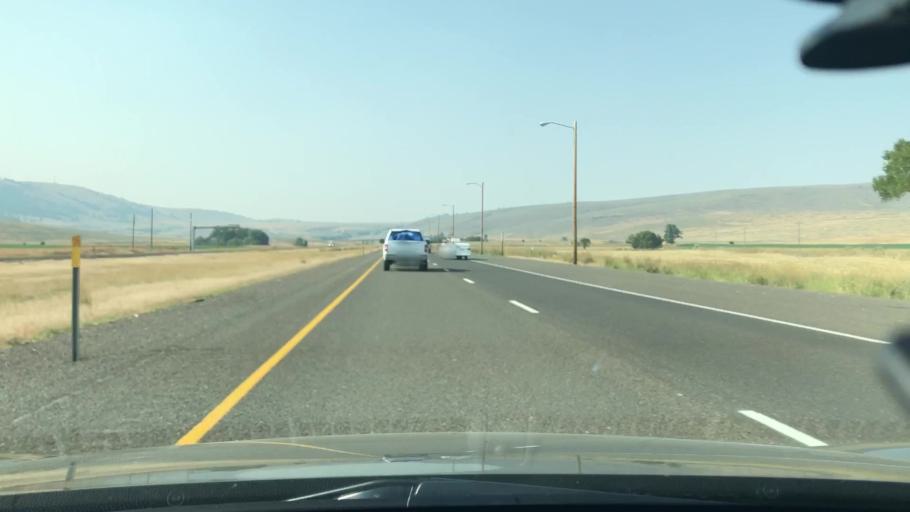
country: US
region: Oregon
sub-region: Union County
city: Union
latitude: 45.1126
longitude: -117.9585
